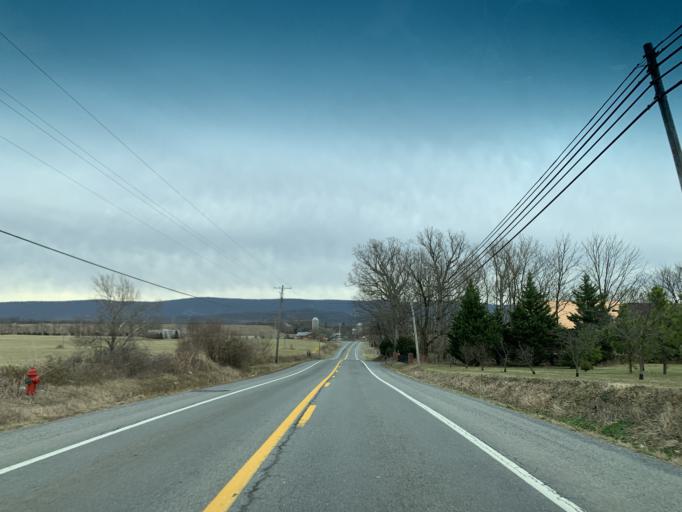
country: US
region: West Virginia
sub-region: Jefferson County
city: Charles Town
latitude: 39.2680
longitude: -77.8386
